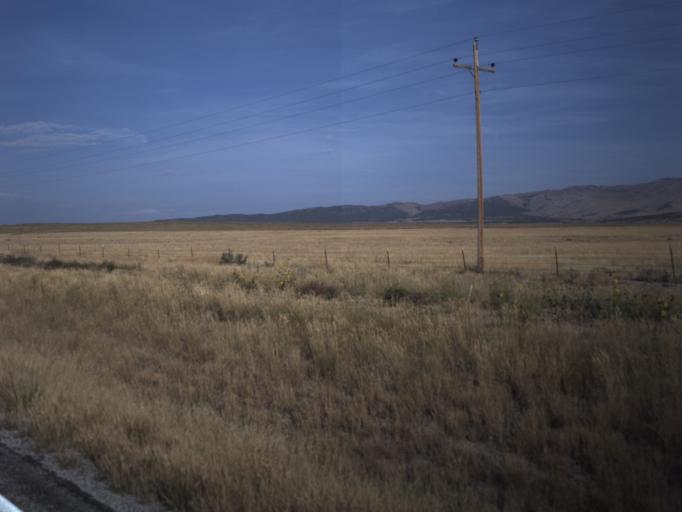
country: US
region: Idaho
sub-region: Oneida County
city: Malad City
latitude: 41.9655
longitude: -113.0341
